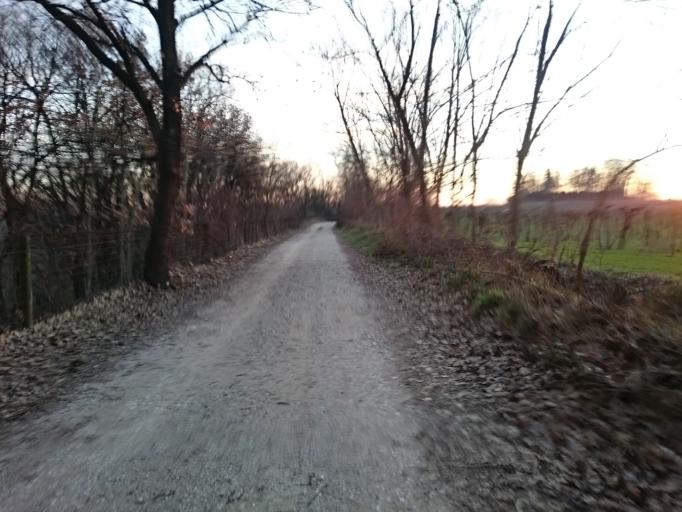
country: IT
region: Veneto
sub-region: Provincia di Verona
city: Castelnuovo del Garda
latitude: 45.4189
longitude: 10.7552
